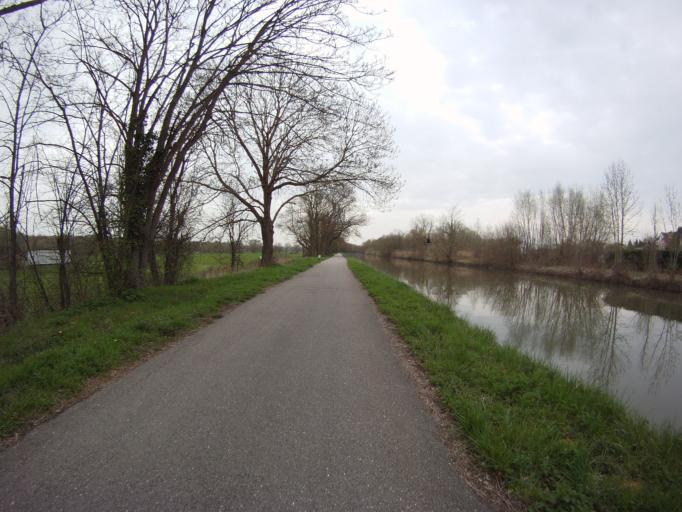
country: FR
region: Lorraine
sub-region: Departement de Meurthe-et-Moselle
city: Jarville-la-Malgrange
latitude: 48.6663
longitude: 6.2175
